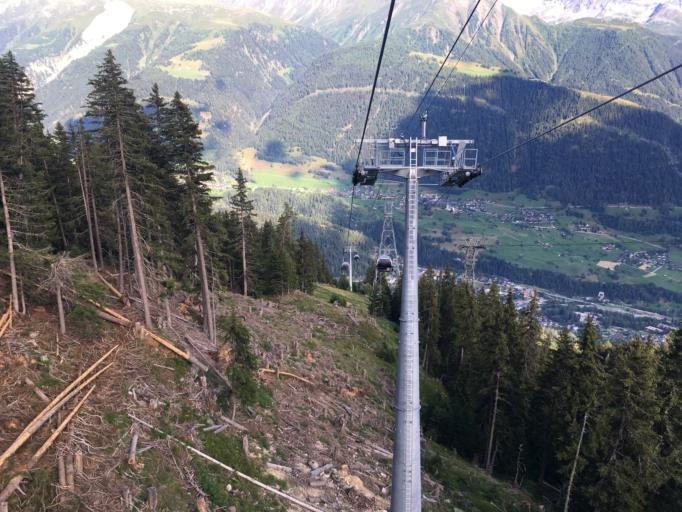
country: CH
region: Valais
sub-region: Goms District
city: Fiesch
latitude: 46.4112
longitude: 8.1123
